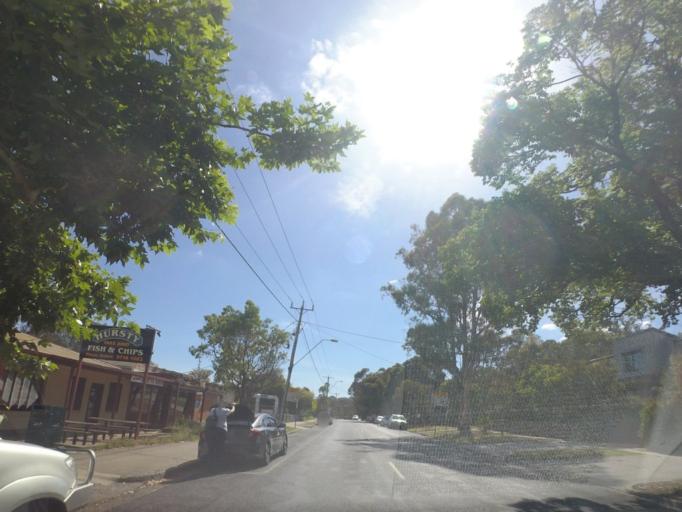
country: AU
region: Victoria
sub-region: Nillumbik
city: Hurstbridge
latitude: -37.6369
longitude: 145.1963
